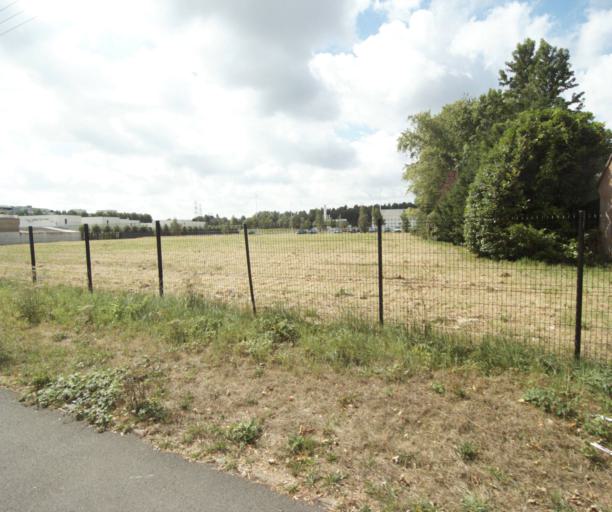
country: FR
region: Nord-Pas-de-Calais
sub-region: Departement du Nord
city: Croix
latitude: 50.6546
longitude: 3.1540
